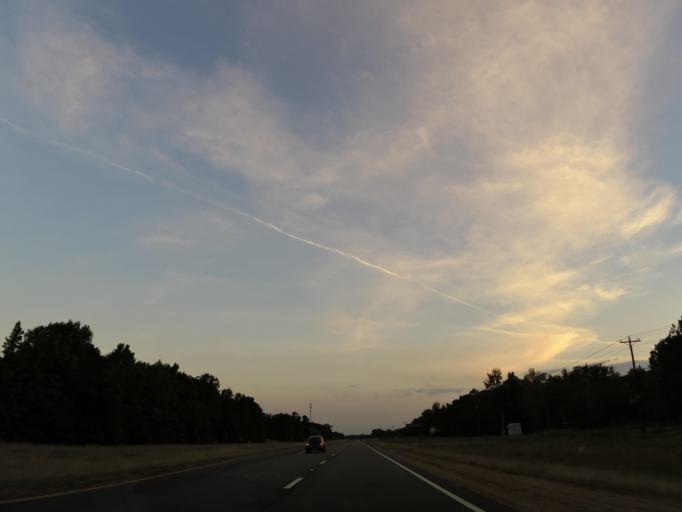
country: US
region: Mississippi
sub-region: Kemper County
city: De Kalb
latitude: 32.7791
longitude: -88.4608
